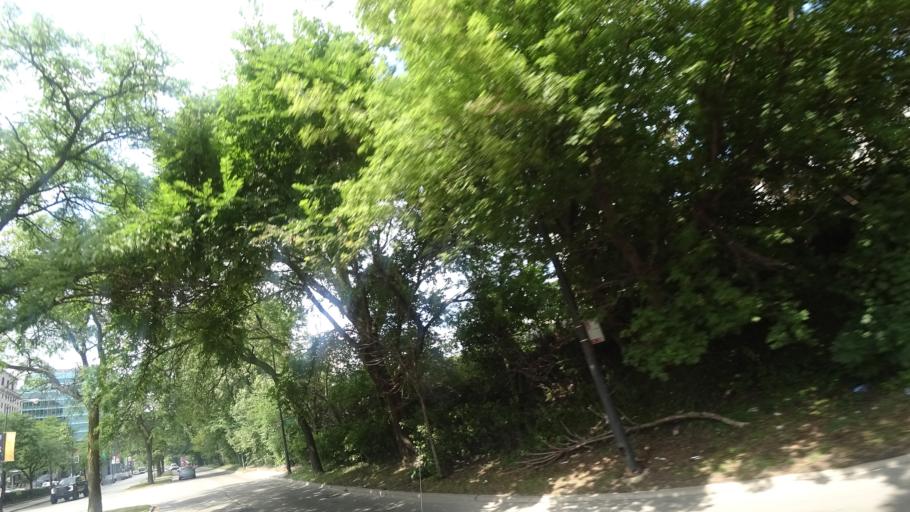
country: US
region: Illinois
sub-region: Cook County
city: Chicago
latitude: 41.7977
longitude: -87.5872
